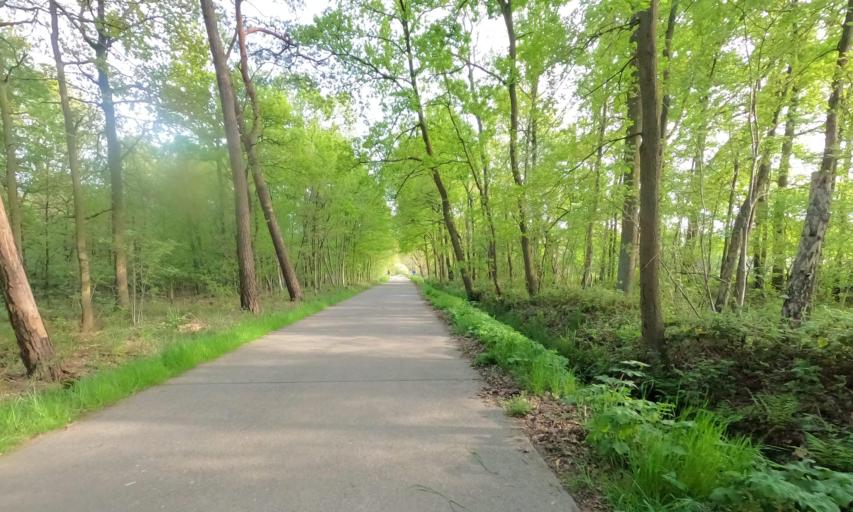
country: BE
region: Flanders
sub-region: Provincie Antwerpen
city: Zandhoven
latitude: 51.2554
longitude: 4.6543
